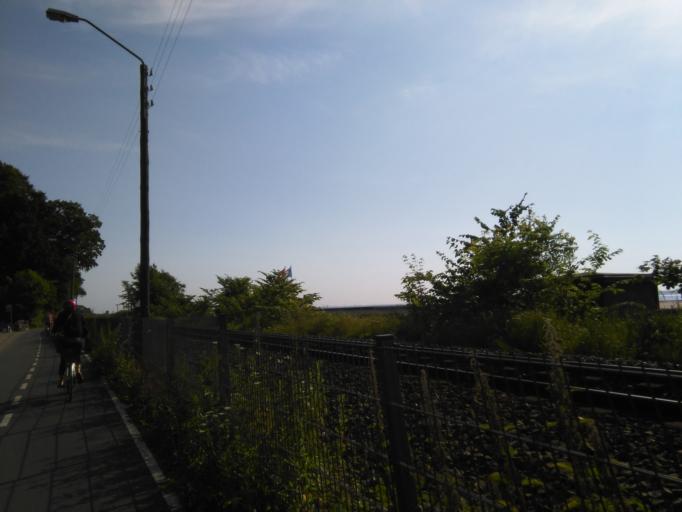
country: DK
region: Central Jutland
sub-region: Arhus Kommune
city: Arhus
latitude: 56.1763
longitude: 10.2303
